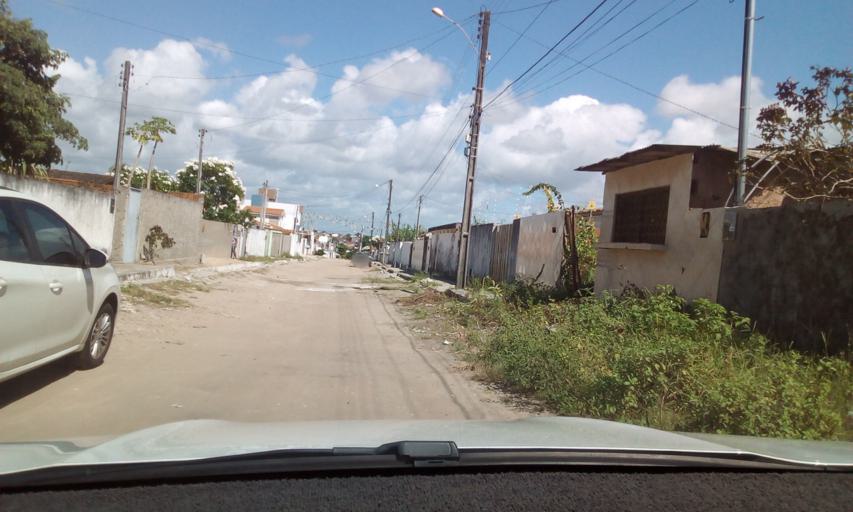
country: BR
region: Paraiba
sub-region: Joao Pessoa
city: Joao Pessoa
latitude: -7.2026
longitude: -34.8330
